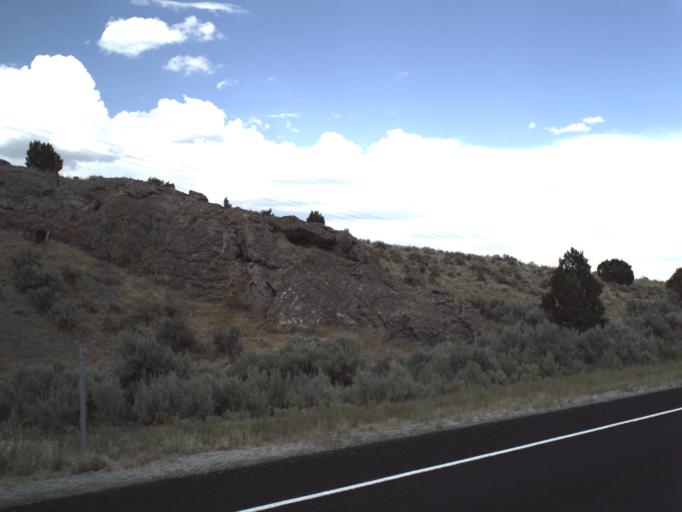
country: US
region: Idaho
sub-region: Minidoka County
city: Rupert
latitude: 41.9728
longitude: -113.1535
